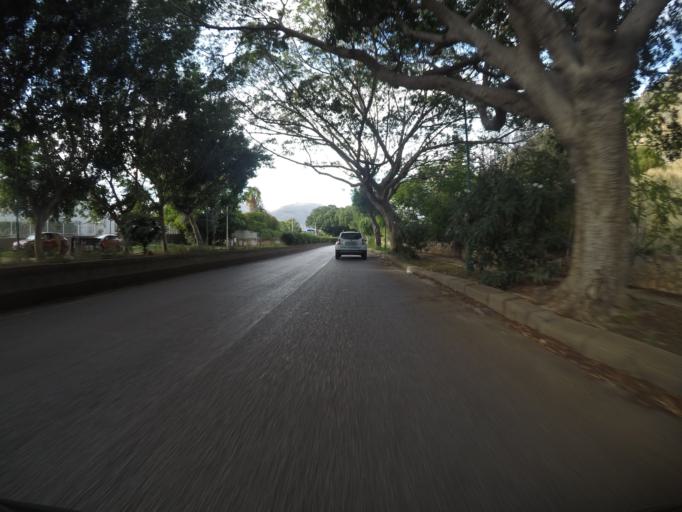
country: IT
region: Sicily
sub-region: Palermo
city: Palermo
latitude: 38.1807
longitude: 13.3346
